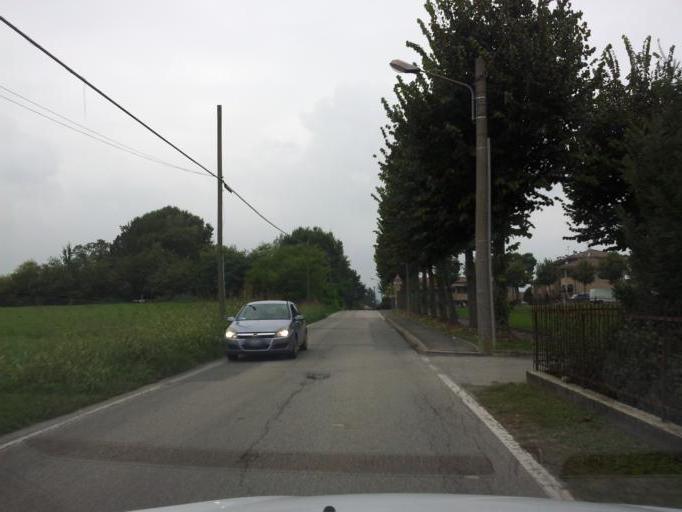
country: IT
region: Lombardy
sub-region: Provincia di Varese
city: Sesto Calende
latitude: 45.7306
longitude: 8.6438
